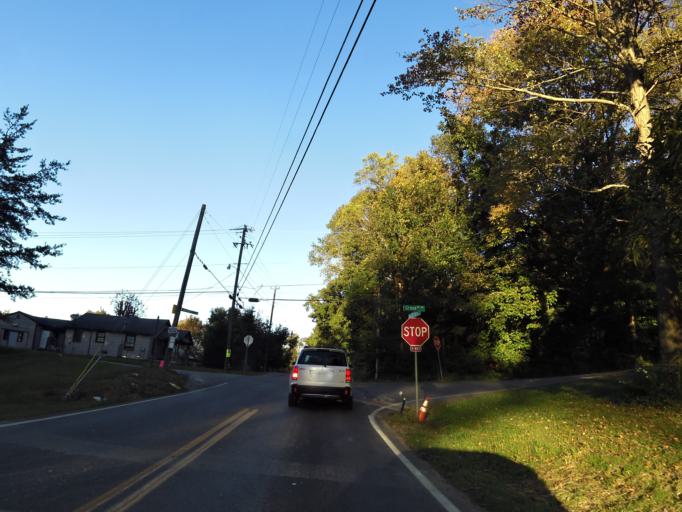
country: US
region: Tennessee
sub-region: Knox County
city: Knoxville
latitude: 36.0465
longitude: -83.9464
